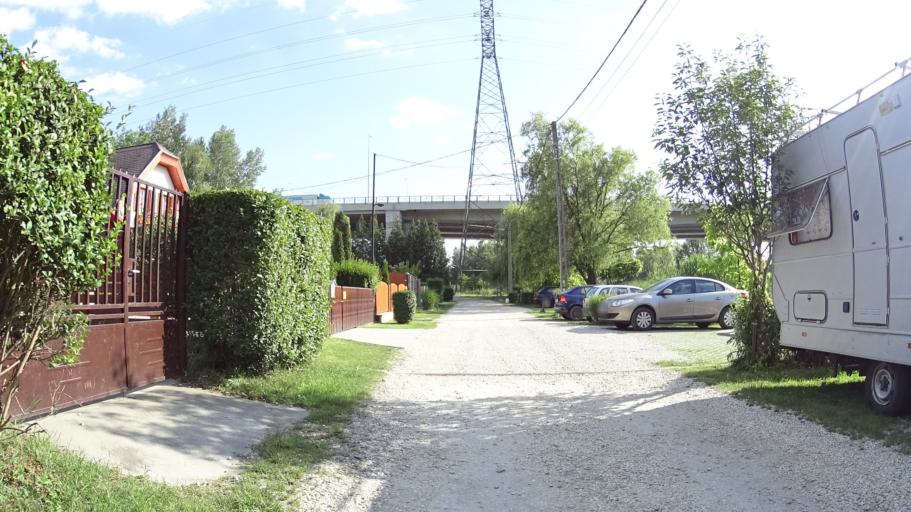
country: HU
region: Pest
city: Dunaharaszti
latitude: 47.3719
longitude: 19.0941
